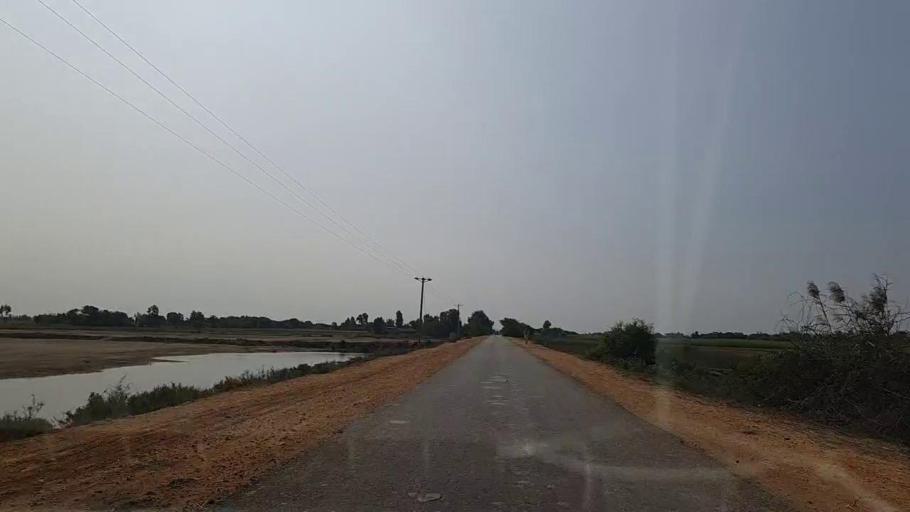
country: PK
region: Sindh
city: Chuhar Jamali
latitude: 24.3619
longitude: 67.9609
